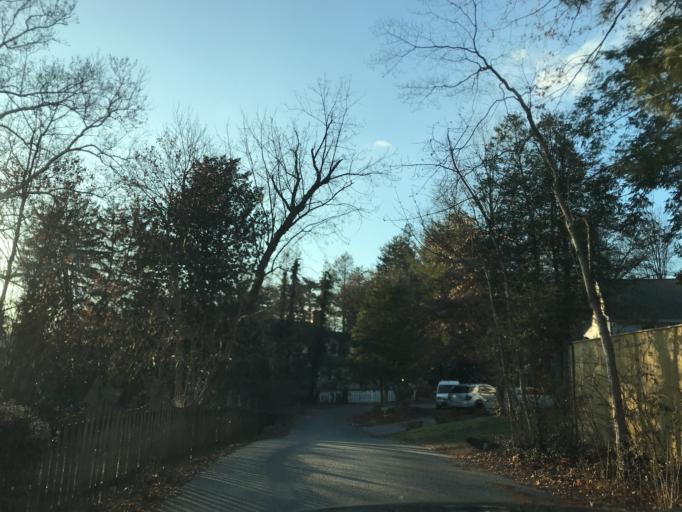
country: US
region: Maryland
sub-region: Baltimore County
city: Lutherville
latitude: 39.3971
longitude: -76.6409
